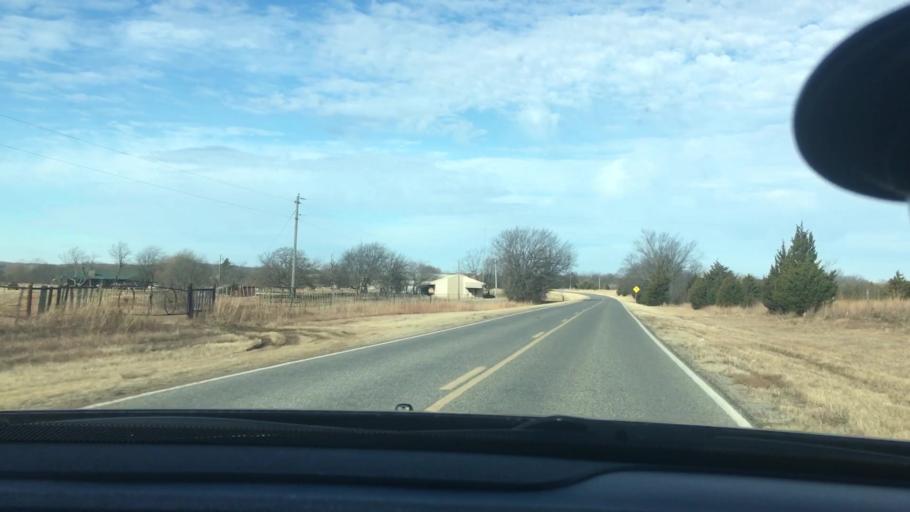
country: US
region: Oklahoma
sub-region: Seminole County
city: Konawa
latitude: 34.9822
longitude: -96.7932
